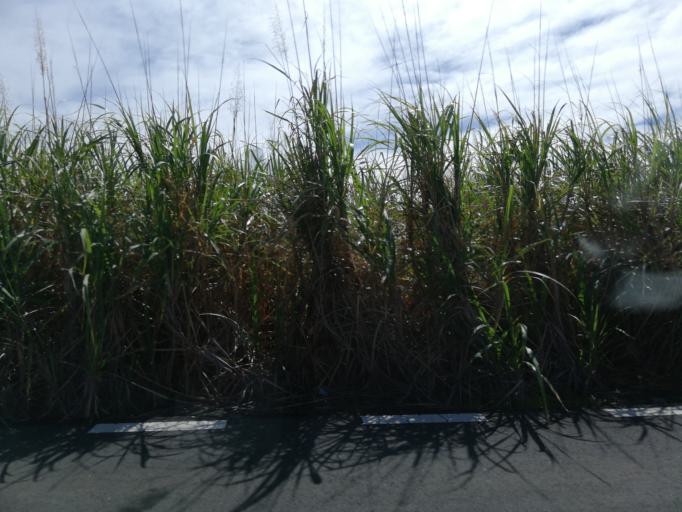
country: MU
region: Grand Port
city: Plaine Magnien
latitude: -20.4535
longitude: 57.6747
